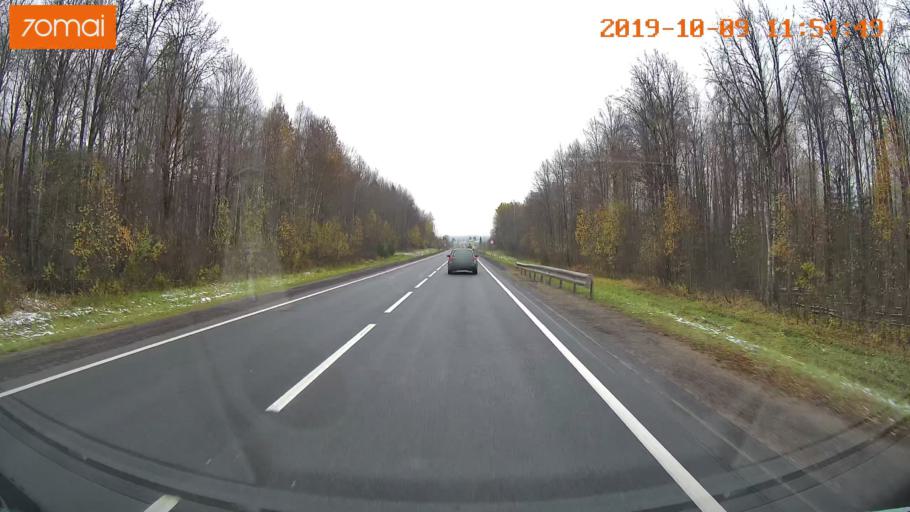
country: RU
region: Vologda
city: Gryazovets
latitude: 58.7548
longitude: 40.2832
